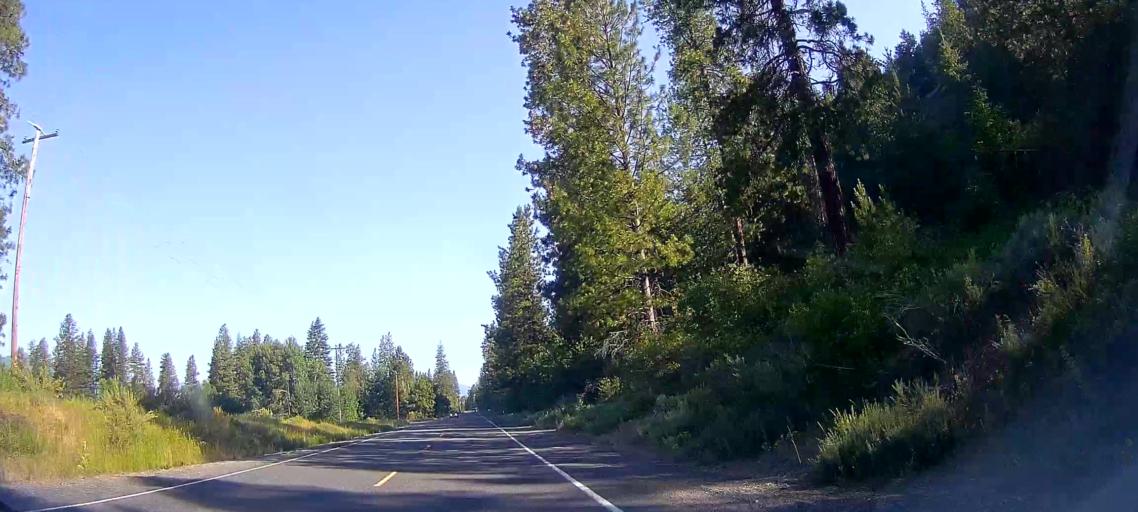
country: US
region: Oregon
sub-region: Klamath County
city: Klamath Falls
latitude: 42.6356
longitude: -121.9387
